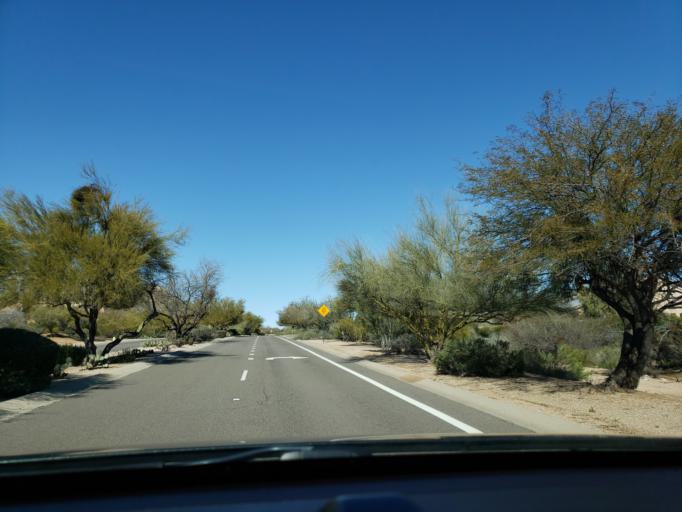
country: US
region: Arizona
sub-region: Maricopa County
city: Carefree
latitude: 33.7087
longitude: -111.8300
